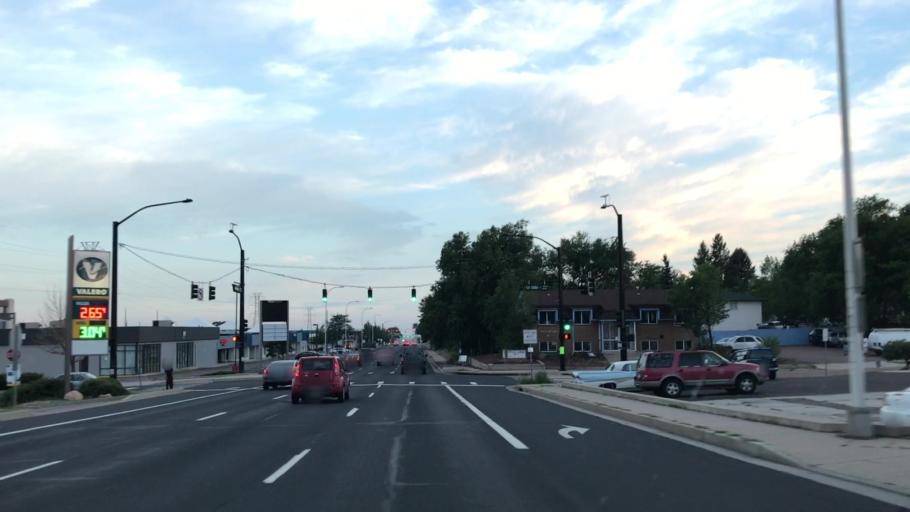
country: US
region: Colorado
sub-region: El Paso County
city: Cimarron Hills
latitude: 38.8577
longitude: -104.7574
